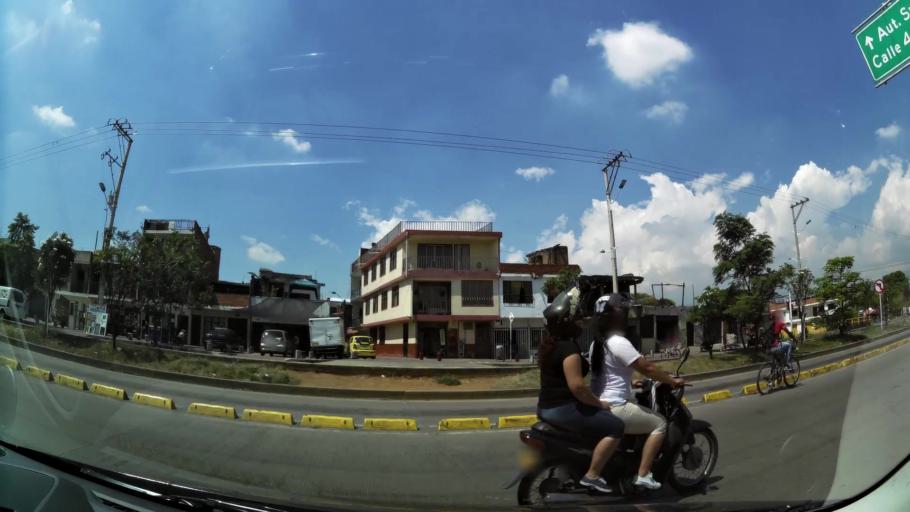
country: CO
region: Valle del Cauca
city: Cali
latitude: 3.4266
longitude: -76.5045
